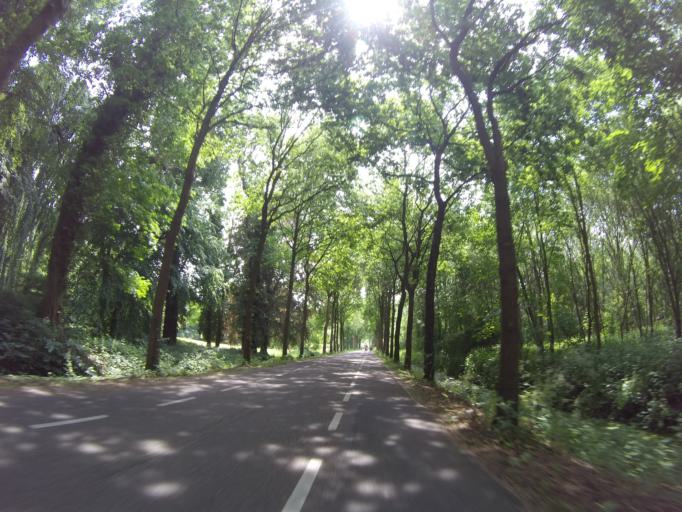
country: NL
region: Utrecht
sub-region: Gemeente Bunnik
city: Bunnik
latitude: 52.0748
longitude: 5.1975
